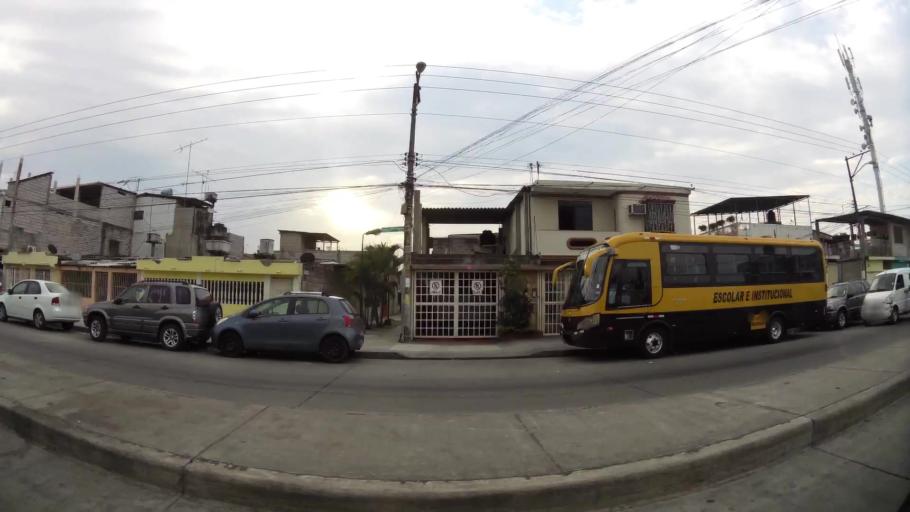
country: EC
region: Guayas
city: Guayaquil
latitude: -2.2551
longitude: -79.8834
